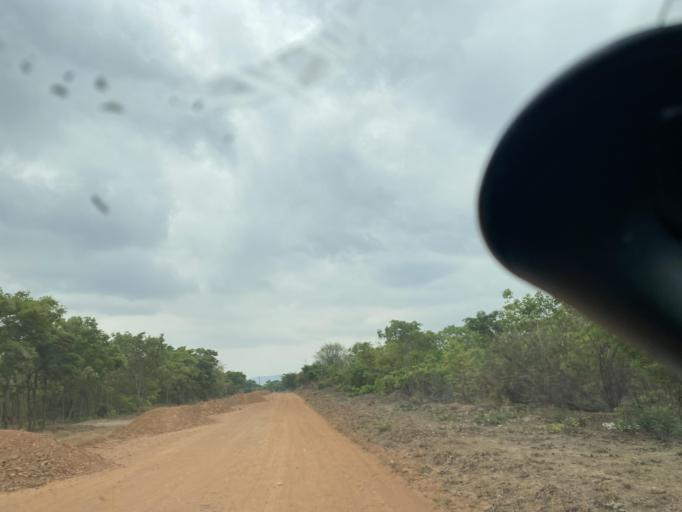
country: ZM
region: Lusaka
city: Chongwe
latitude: -15.2469
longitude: 28.7261
